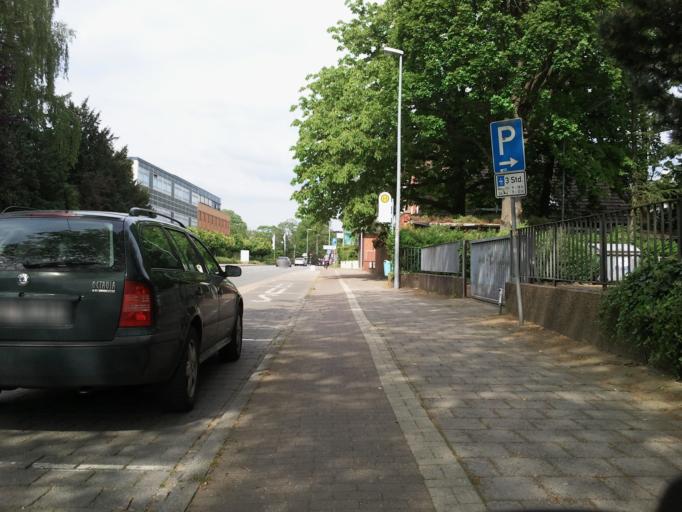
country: DE
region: Lower Saxony
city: Nienburg
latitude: 52.6452
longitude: 9.2098
